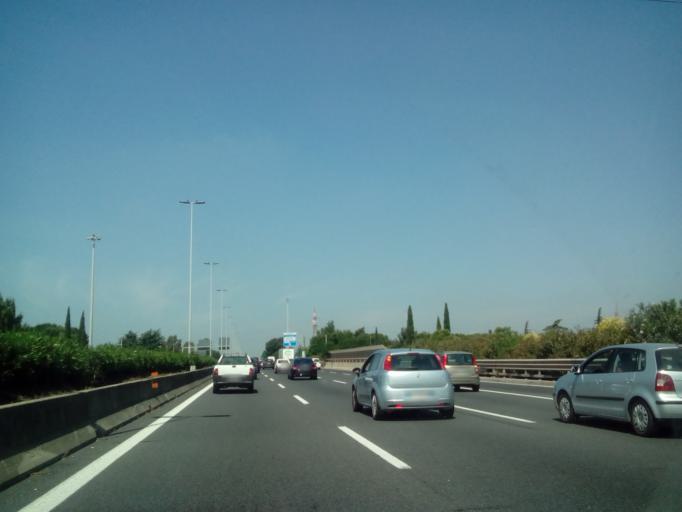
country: IT
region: Latium
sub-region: Citta metropolitana di Roma Capitale
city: Selcetta
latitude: 41.7974
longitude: 12.4818
